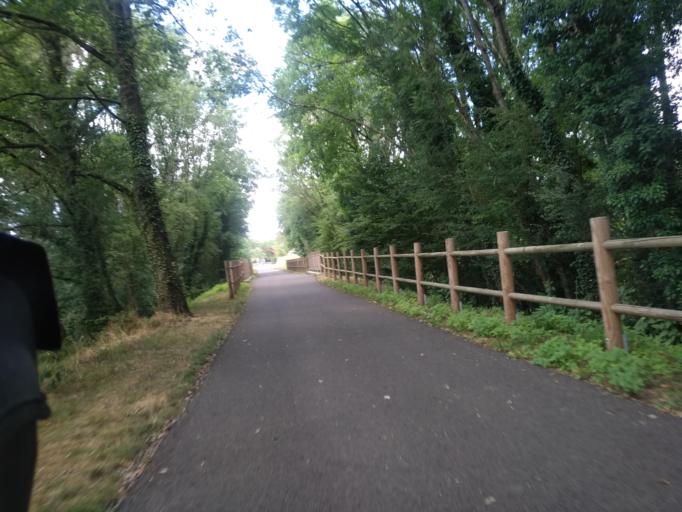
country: FR
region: Rhone-Alpes
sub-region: Departement de la Loire
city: Briennon
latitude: 46.2010
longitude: 4.0800
